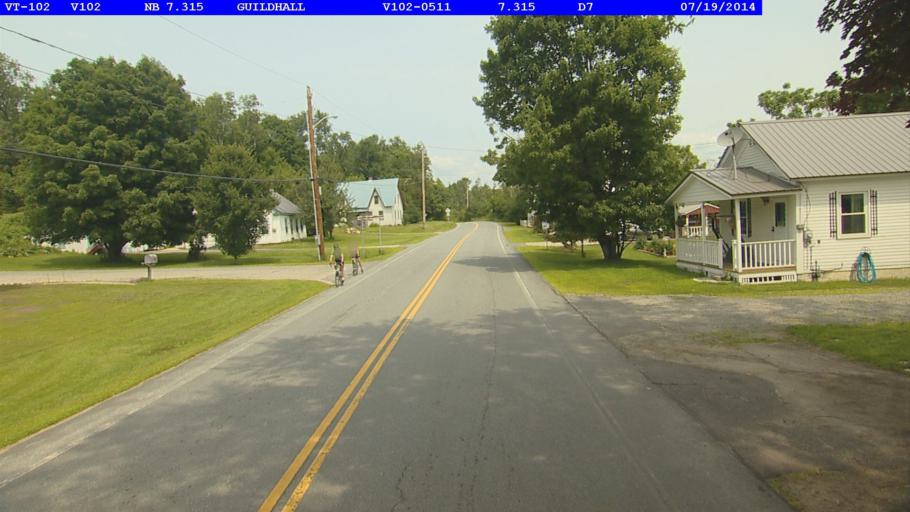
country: US
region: Vermont
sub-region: Essex County
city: Guildhall
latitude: 44.5654
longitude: -71.5603
